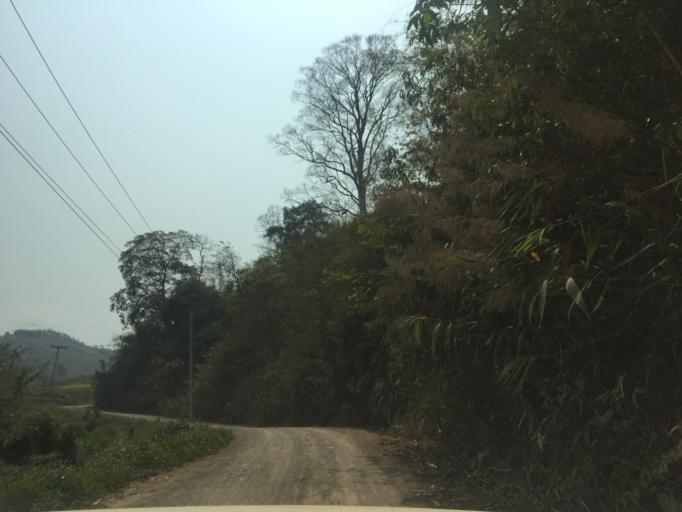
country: LA
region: Loungnamtha
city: Muang Nale
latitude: 20.2992
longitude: 101.6614
